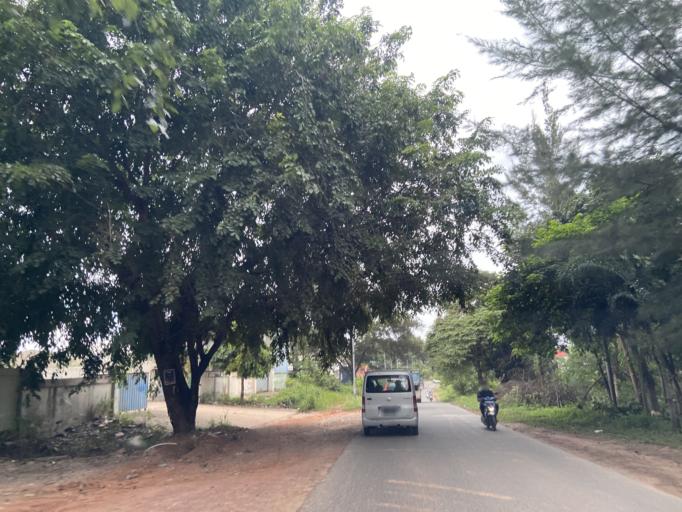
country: SG
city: Singapore
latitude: 1.1081
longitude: 104.0467
